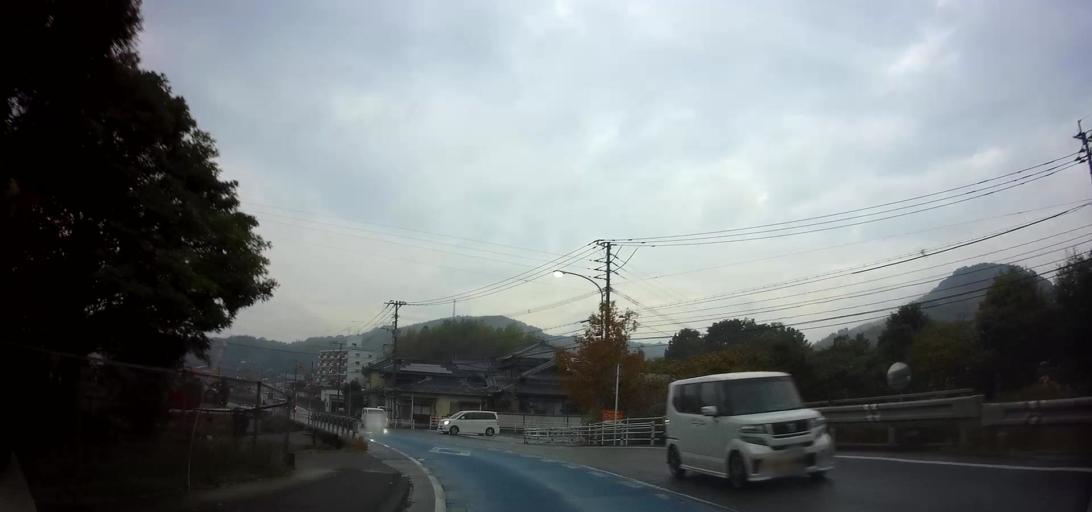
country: JP
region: Nagasaki
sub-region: Isahaya-shi
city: Isahaya
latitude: 32.8496
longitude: 130.0095
